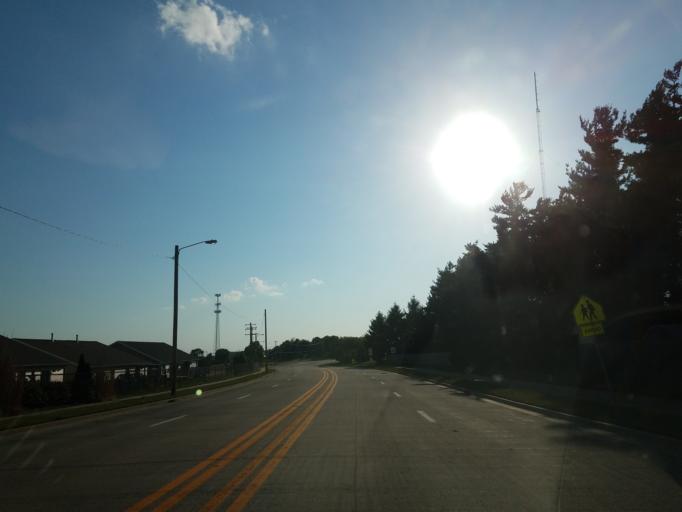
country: US
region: Illinois
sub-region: McLean County
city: Bloomington
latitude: 40.4497
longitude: -89.0091
